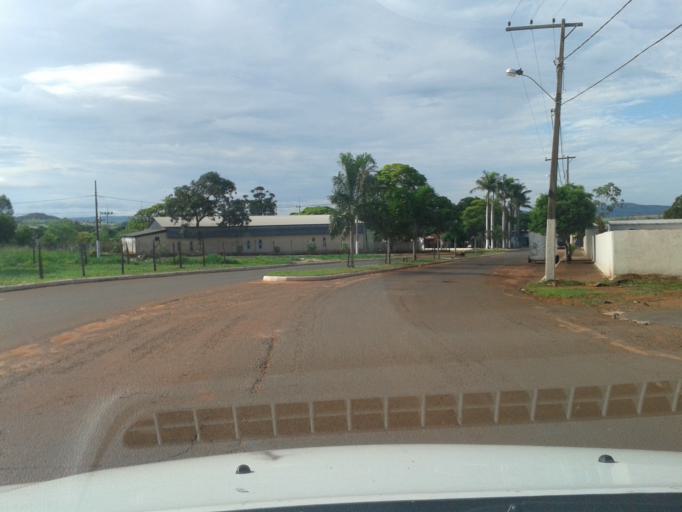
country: BR
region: Minas Gerais
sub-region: Ituiutaba
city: Ituiutaba
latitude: -19.2073
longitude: -49.7845
